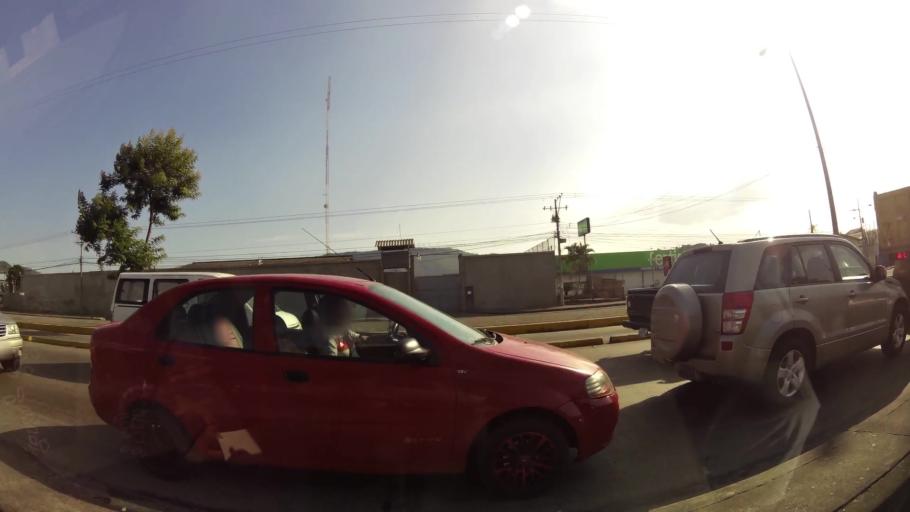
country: EC
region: Guayas
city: Guayaquil
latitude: -2.1537
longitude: -79.9307
